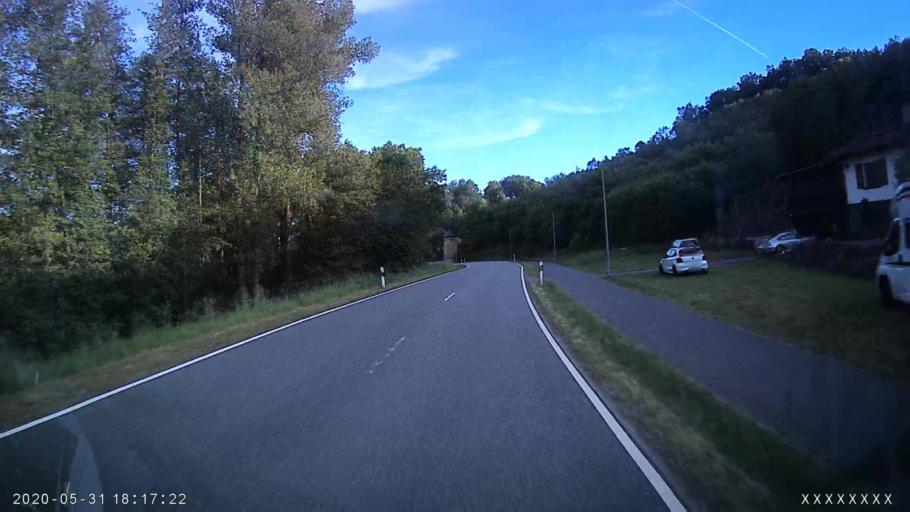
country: DE
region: Hesse
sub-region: Regierungsbezirk Giessen
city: Haiger
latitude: 50.8019
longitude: 8.2015
